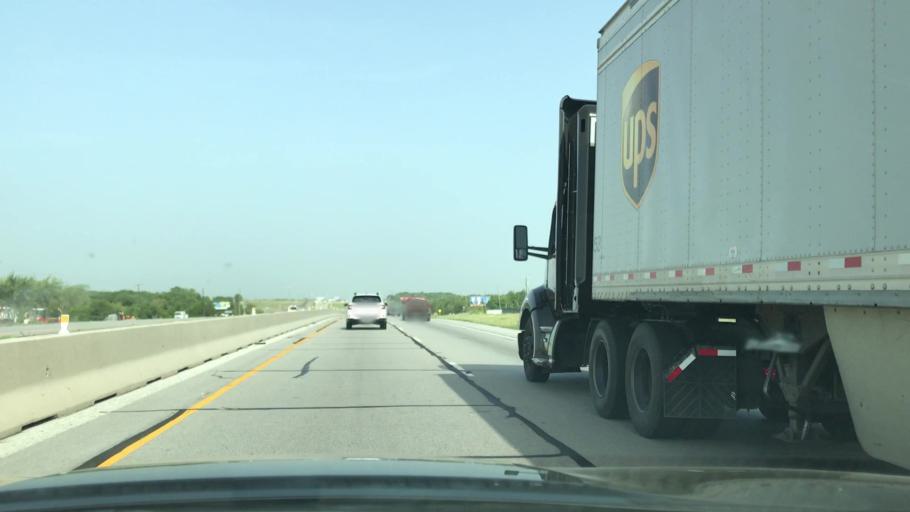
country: US
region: Texas
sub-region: Dallas County
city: Sunnyvale
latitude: 32.7832
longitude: -96.5513
